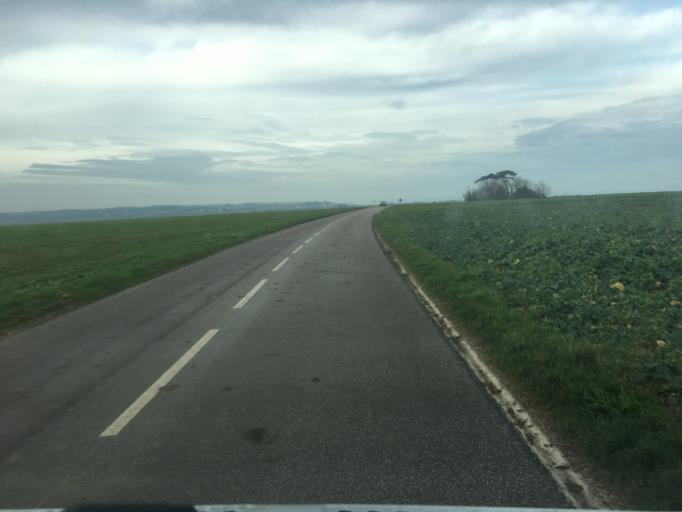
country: FR
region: Lower Normandy
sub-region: Departement du Calvados
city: Ver-sur-Mer
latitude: 49.3211
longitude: -0.5559
